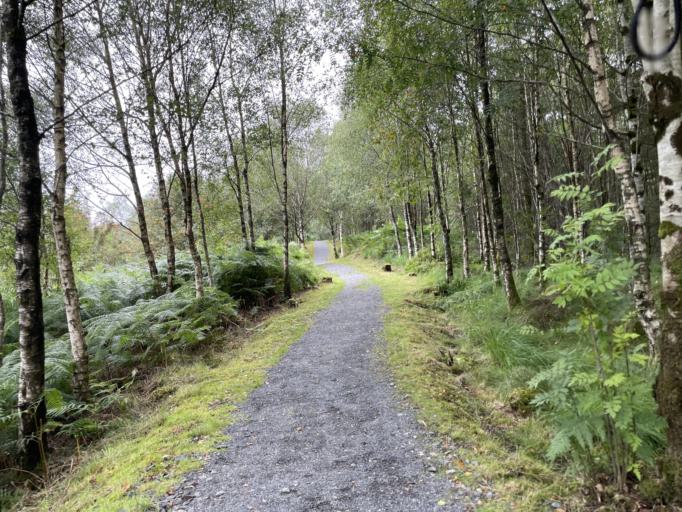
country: GB
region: Scotland
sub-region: Dumfries and Galloway
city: Newton Stewart
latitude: 55.0812
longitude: -4.5093
